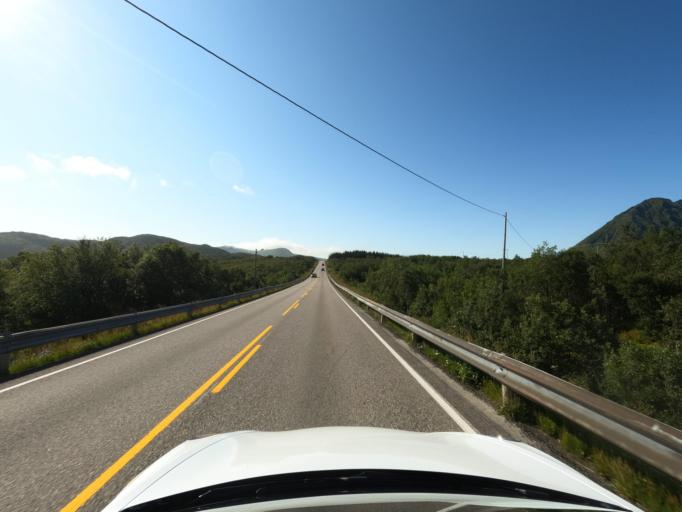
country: NO
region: Nordland
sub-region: Vestvagoy
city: Evjen
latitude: 68.2596
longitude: 14.0055
